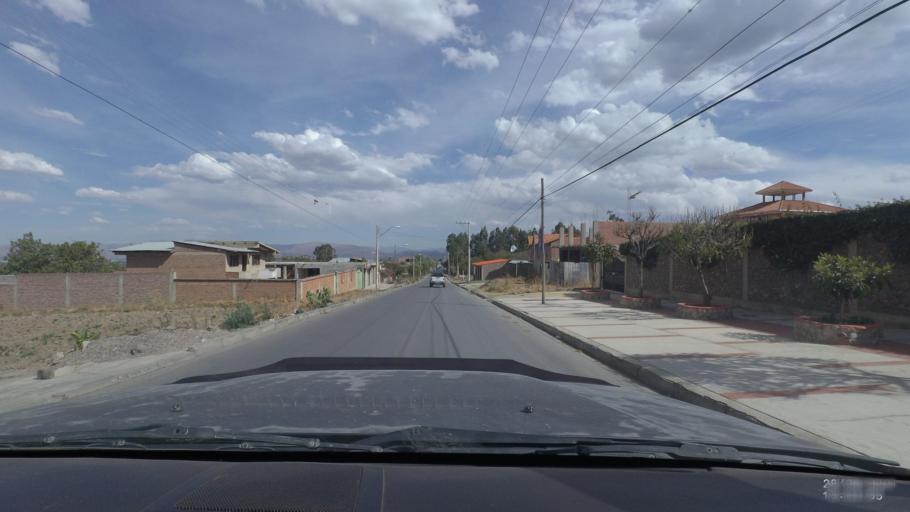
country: BO
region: Cochabamba
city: Cochabamba
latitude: -17.3221
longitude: -66.2817
